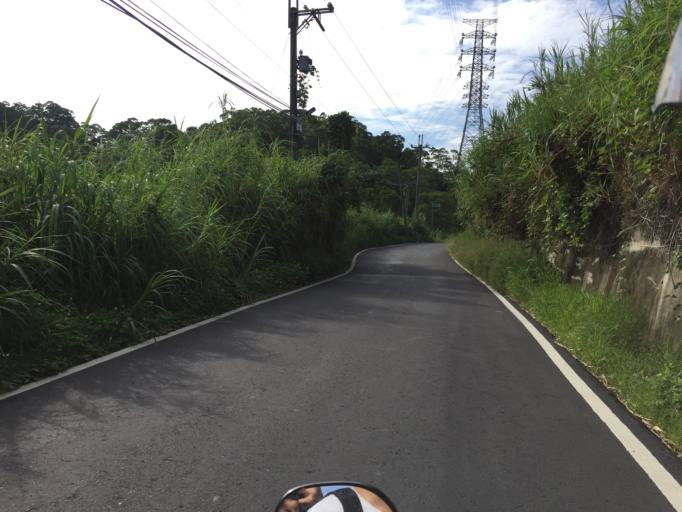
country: TW
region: Taiwan
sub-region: Hsinchu
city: Hsinchu
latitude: 24.7660
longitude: 120.9403
